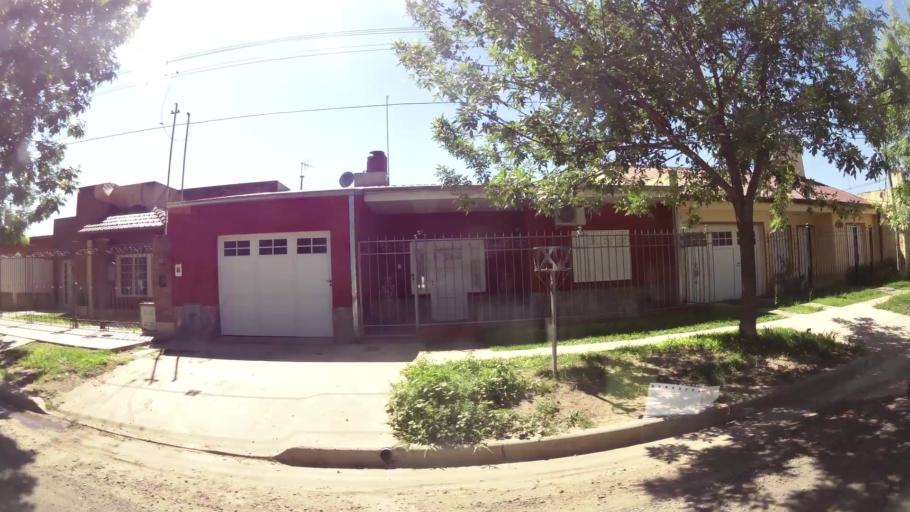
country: AR
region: Santa Fe
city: Esperanza
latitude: -31.4329
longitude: -60.9243
